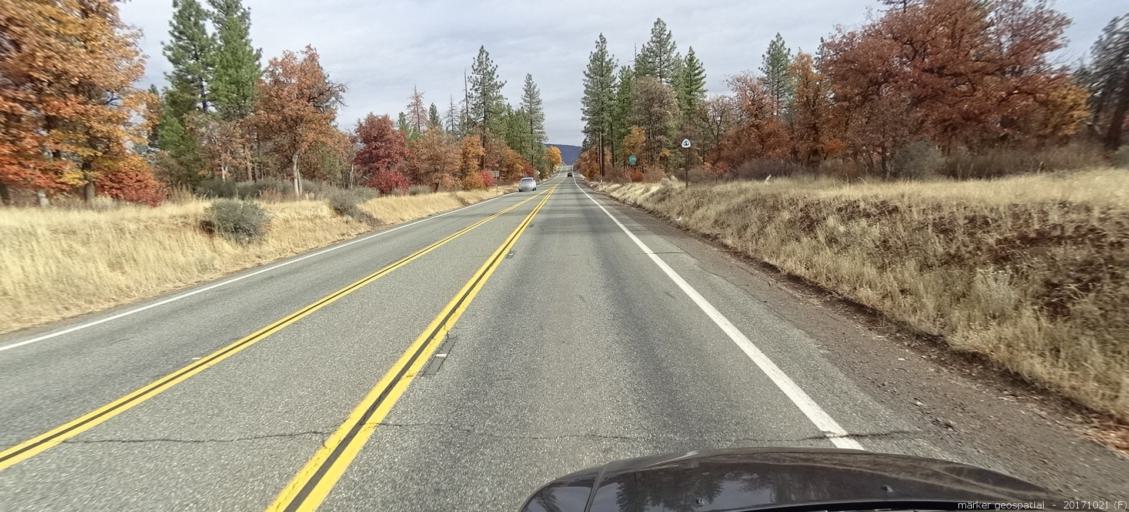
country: US
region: California
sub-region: Shasta County
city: Burney
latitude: 40.9626
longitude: -121.5782
